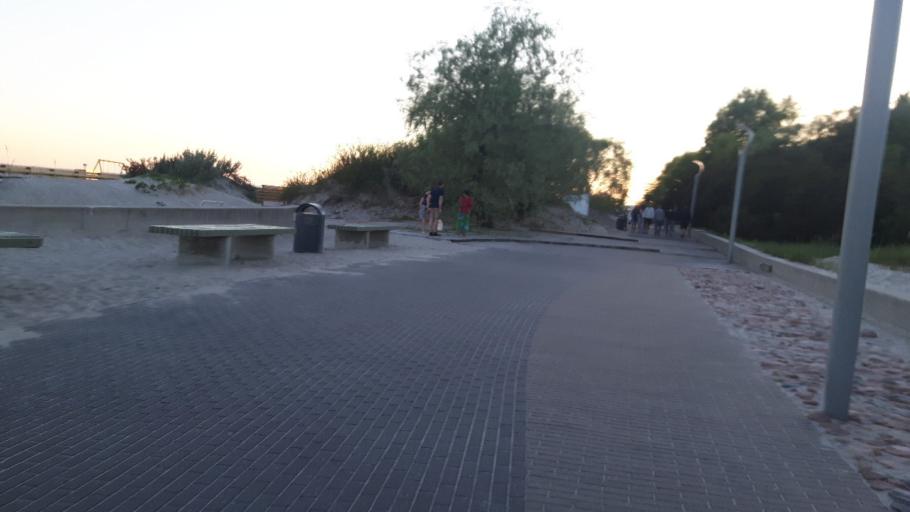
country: EE
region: Paernumaa
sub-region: Paernu linn
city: Parnu
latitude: 58.3723
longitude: 24.5055
